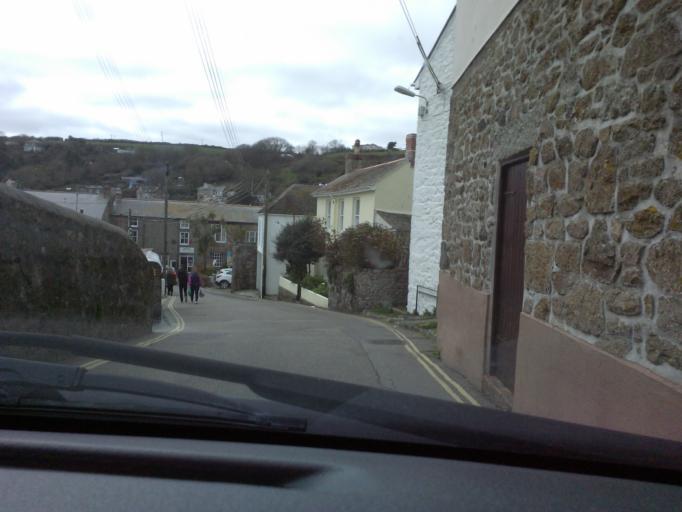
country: GB
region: England
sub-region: Cornwall
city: Penzance
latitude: 50.0845
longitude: -5.5379
